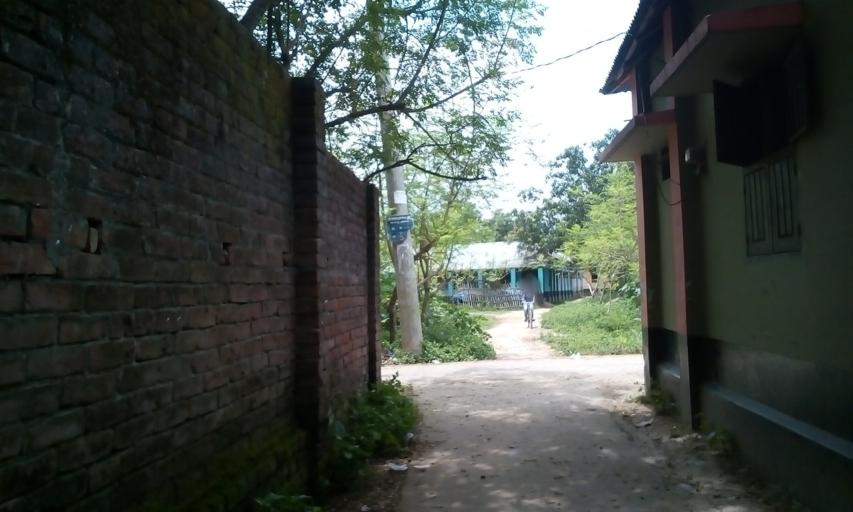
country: IN
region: West Bengal
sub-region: Dakshin Dinajpur
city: Balurghat
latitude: 25.3815
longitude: 88.9960
